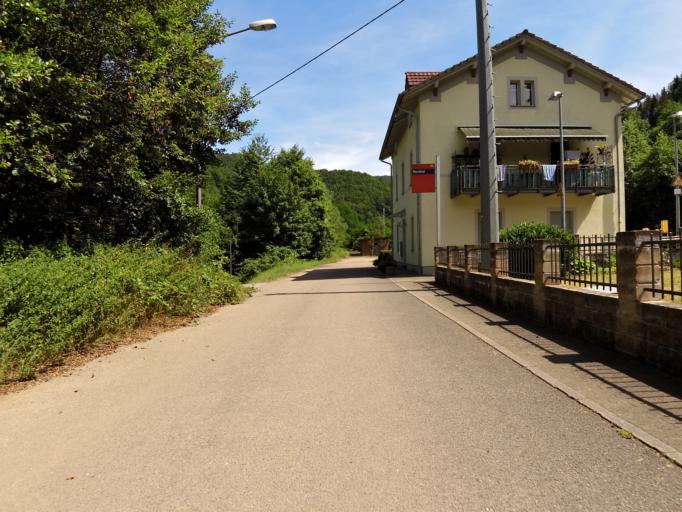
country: DE
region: Rheinland-Pfalz
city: Rinnthal
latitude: 49.2173
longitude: 7.9278
